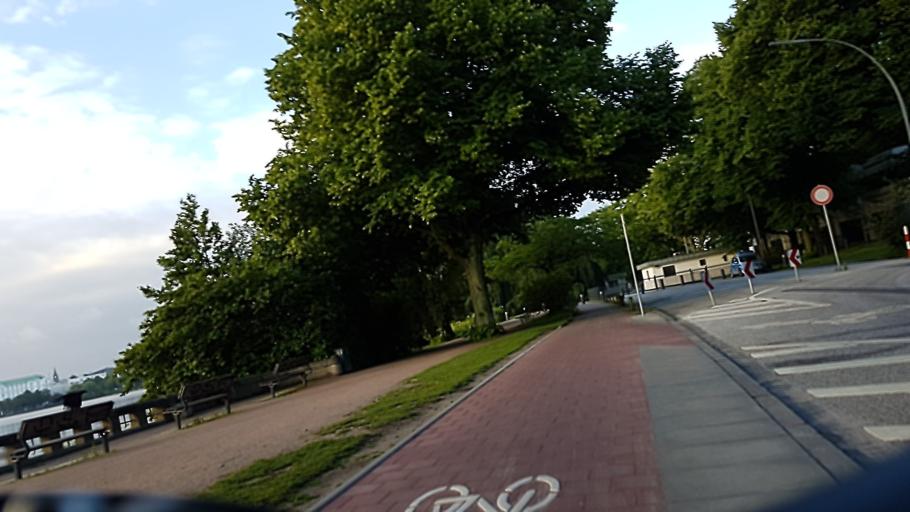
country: DE
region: Hamburg
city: Altstadt
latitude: 53.5634
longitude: 9.9980
